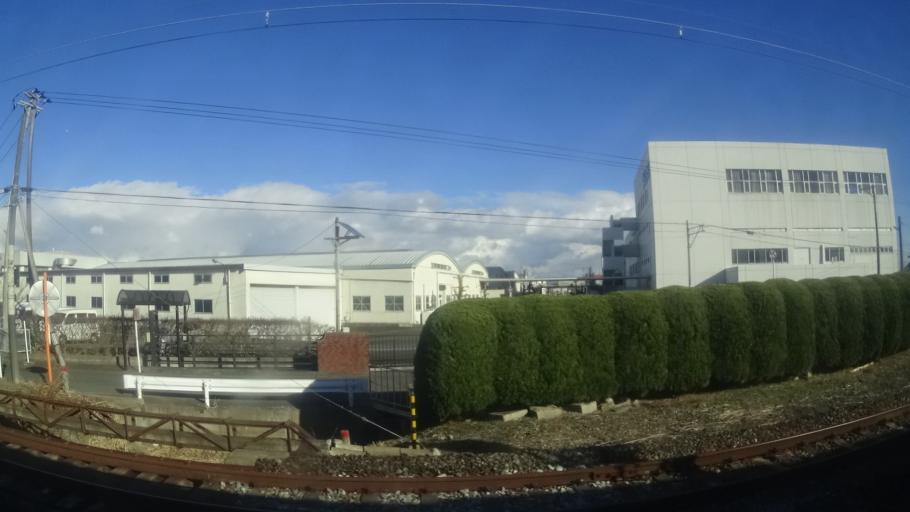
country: JP
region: Miyagi
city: Marumori
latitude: 37.8050
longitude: 140.9251
